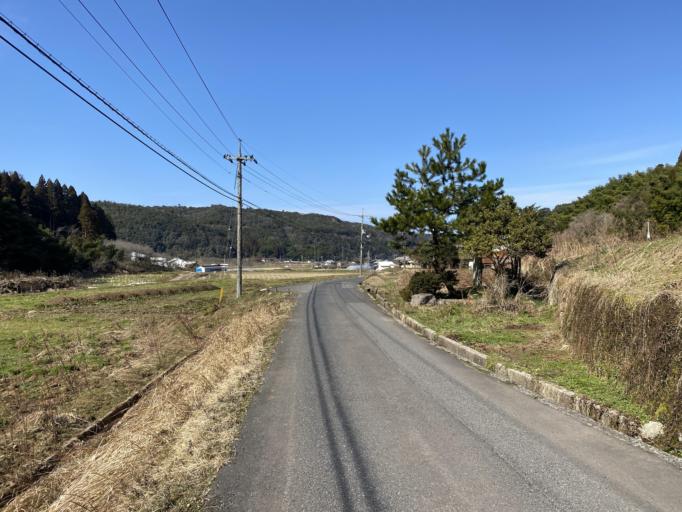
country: JP
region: Tottori
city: Kurayoshi
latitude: 35.4925
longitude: 133.9884
